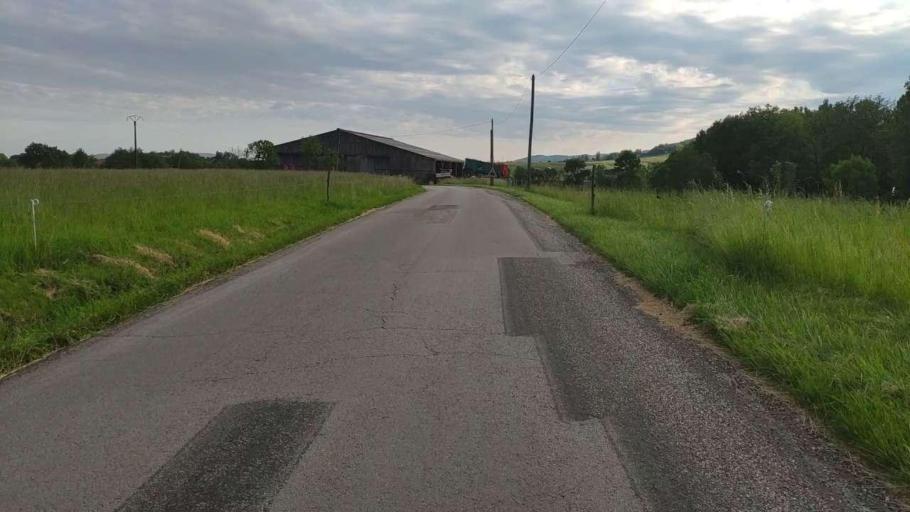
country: FR
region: Franche-Comte
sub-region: Departement du Jura
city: Perrigny
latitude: 46.7216
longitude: 5.5931
